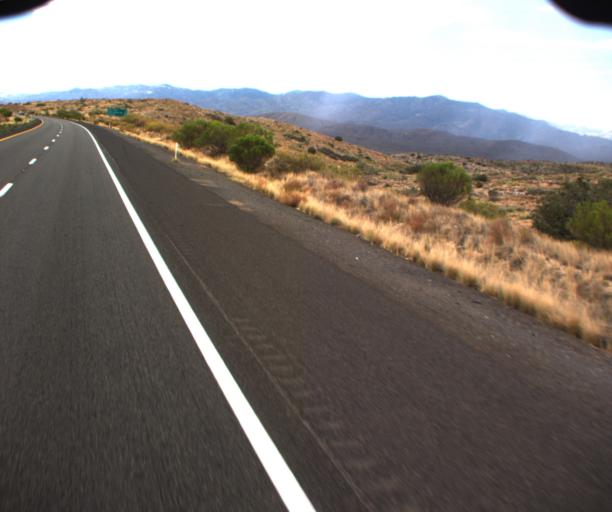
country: US
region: Arizona
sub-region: Yavapai County
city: Cordes Lakes
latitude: 34.2663
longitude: -112.1158
